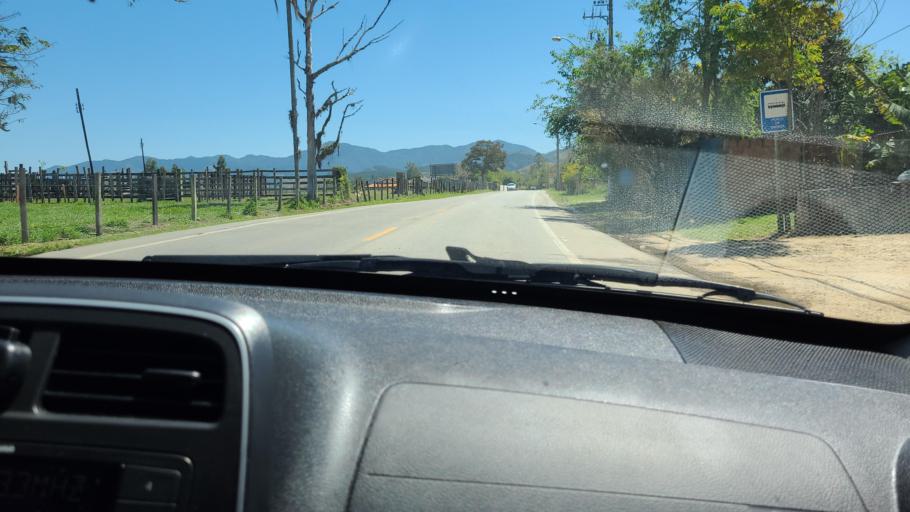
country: BR
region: Sao Paulo
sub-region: Pindamonhangaba
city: Pindamonhangaba
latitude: -22.8884
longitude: -45.5092
